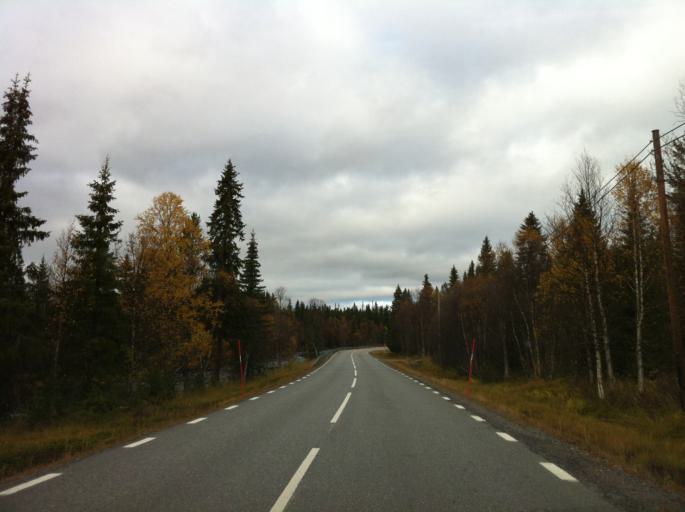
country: NO
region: Hedmark
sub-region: Engerdal
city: Engerdal
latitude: 62.0722
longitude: 12.3109
